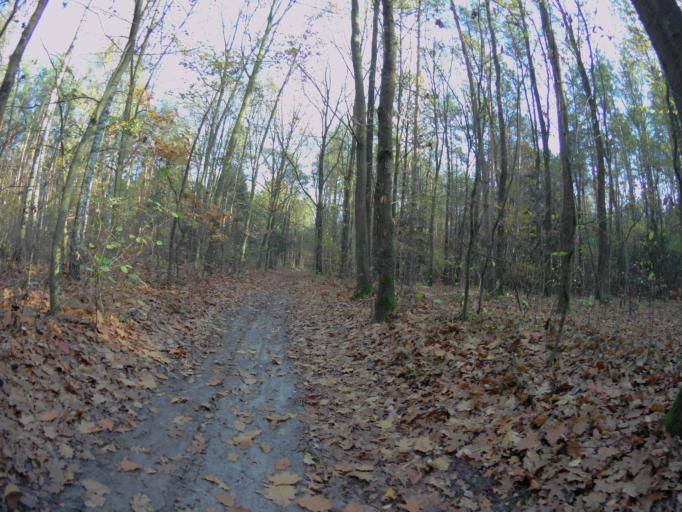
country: PL
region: Subcarpathian Voivodeship
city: Nowa Sarzyna
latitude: 50.3106
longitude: 22.3471
